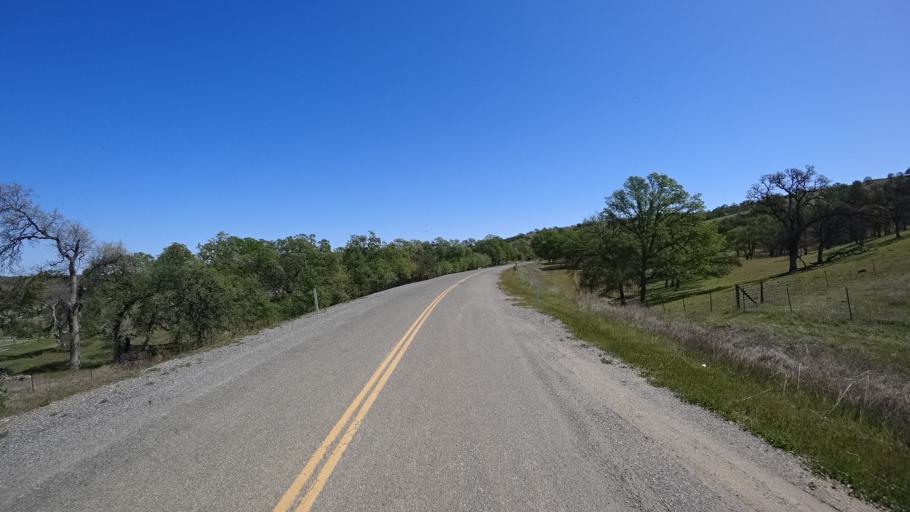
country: US
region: California
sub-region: Glenn County
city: Orland
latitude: 39.7316
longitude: -122.4114
